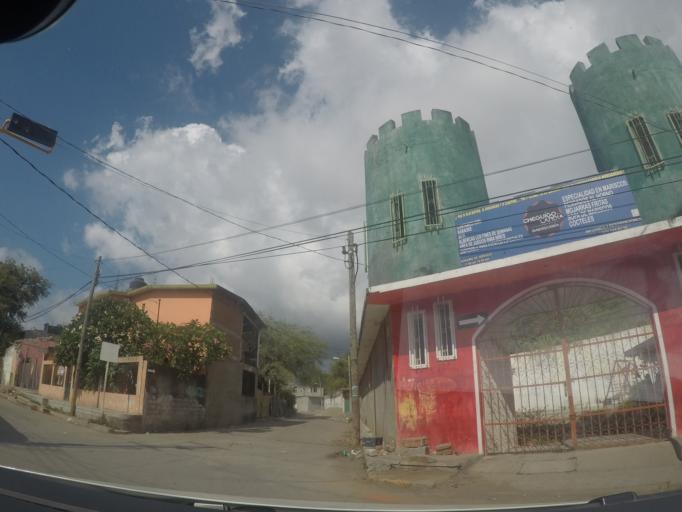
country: MX
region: Oaxaca
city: Juchitan de Zaragoza
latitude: 16.4329
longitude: -95.0264
